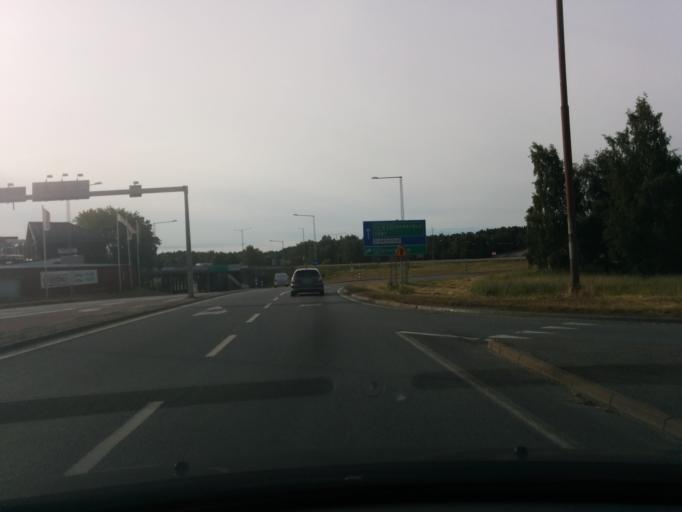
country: SE
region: Stockholm
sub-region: Danderyds Kommun
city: Djursholm
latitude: 59.4104
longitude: 18.0316
